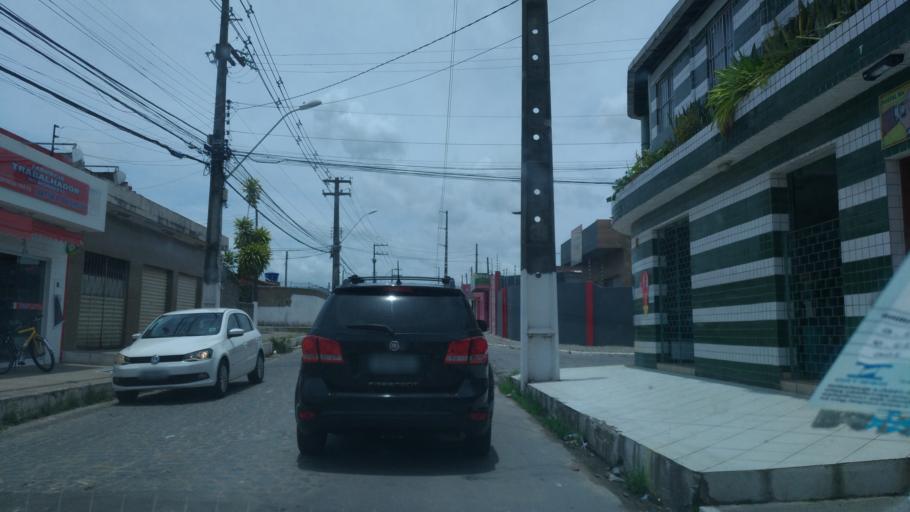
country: BR
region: Alagoas
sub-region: Satuba
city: Satuba
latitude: -9.5634
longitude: -35.7418
